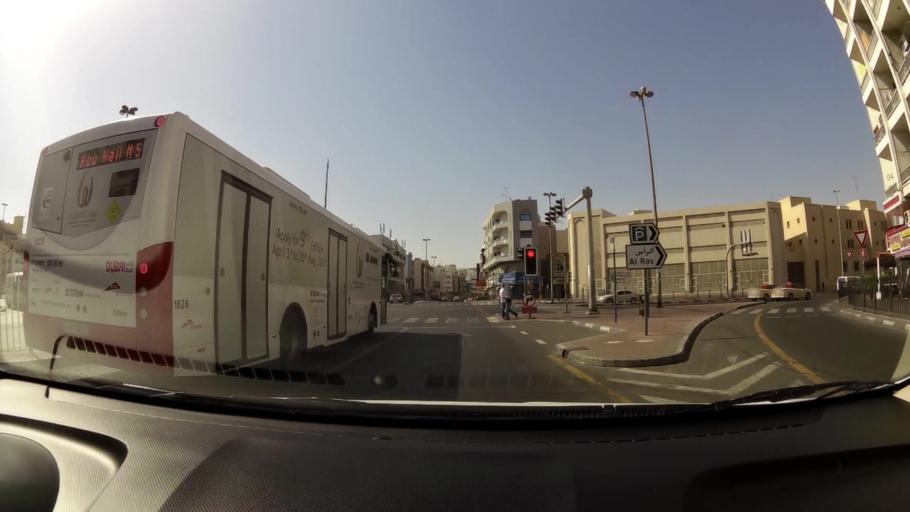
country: AE
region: Ash Shariqah
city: Sharjah
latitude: 25.2738
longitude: 55.3063
